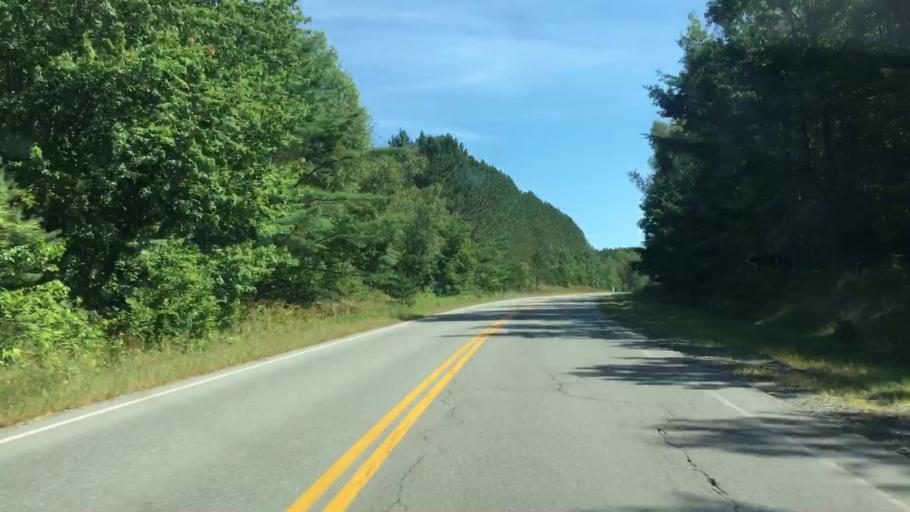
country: US
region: Maine
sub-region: Piscataquis County
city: Milo
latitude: 45.2294
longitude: -68.9349
